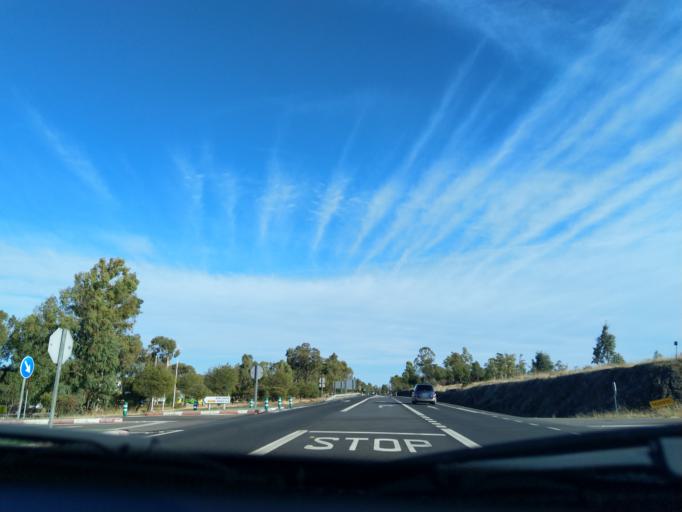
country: ES
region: Extremadura
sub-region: Provincia de Badajoz
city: Berlanga
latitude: 38.2750
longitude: -5.8207
